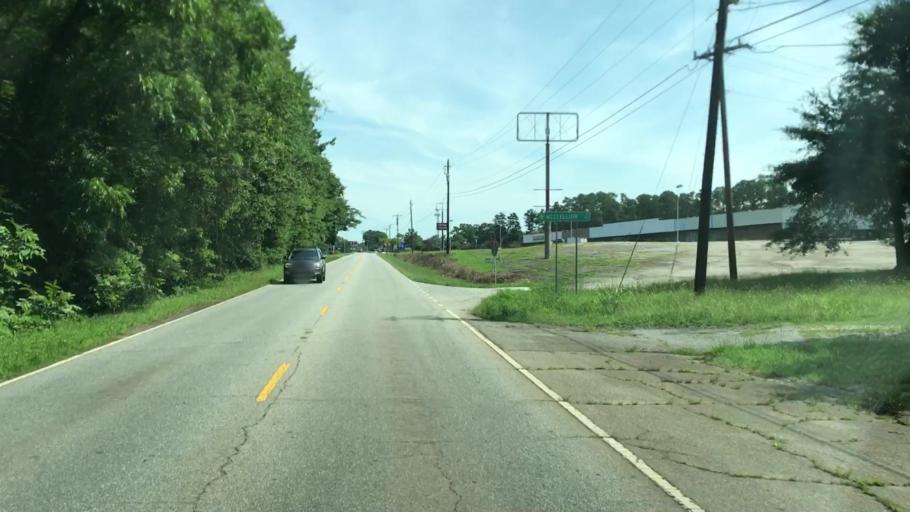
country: US
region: South Carolina
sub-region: Anderson County
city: Williamston
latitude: 34.6396
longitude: -82.4669
